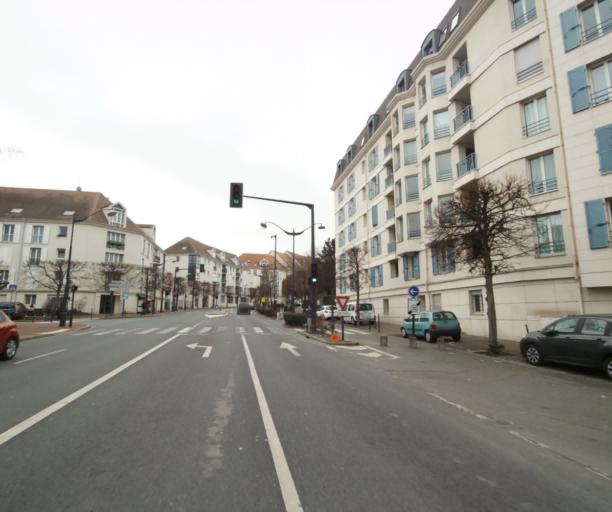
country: FR
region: Ile-de-France
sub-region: Departement des Hauts-de-Seine
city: Rueil-Malmaison
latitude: 48.8789
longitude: 2.1862
